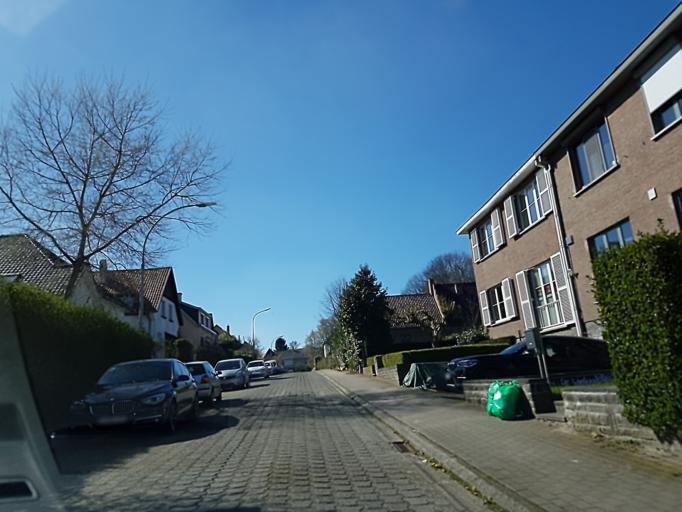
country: BE
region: Flanders
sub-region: Provincie Vlaams-Brabant
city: Dilbeek
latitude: 50.8519
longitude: 4.2654
